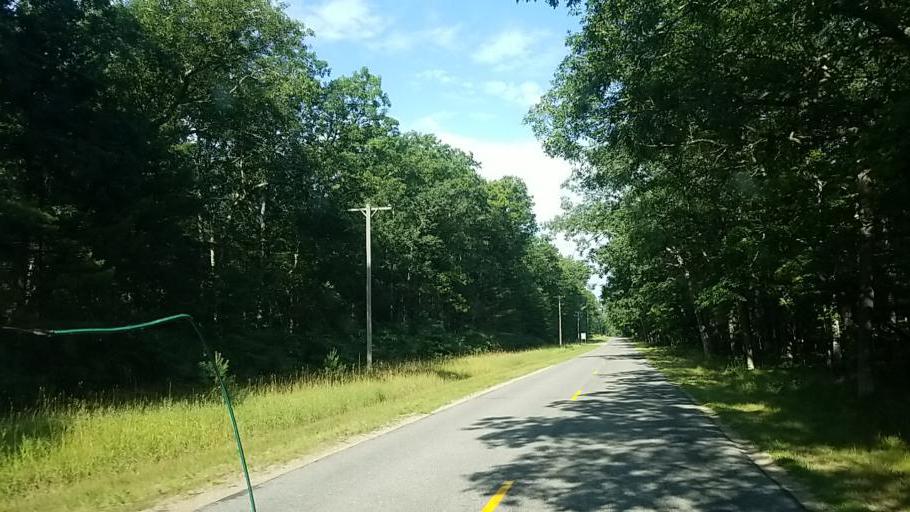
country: US
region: Michigan
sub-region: Muskegon County
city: Lakewood Club
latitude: 43.4623
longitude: -86.2159
